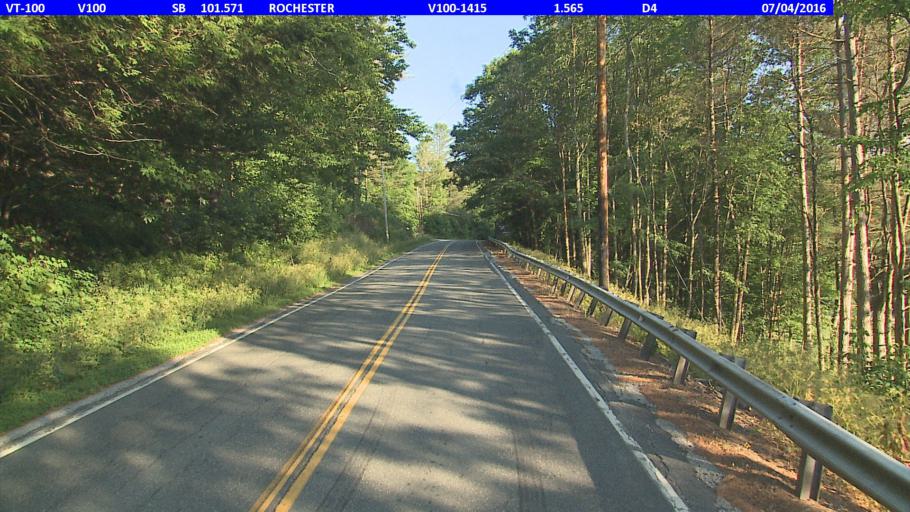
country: US
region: Vermont
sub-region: Orange County
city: Randolph
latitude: 43.8254
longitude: -72.7908
